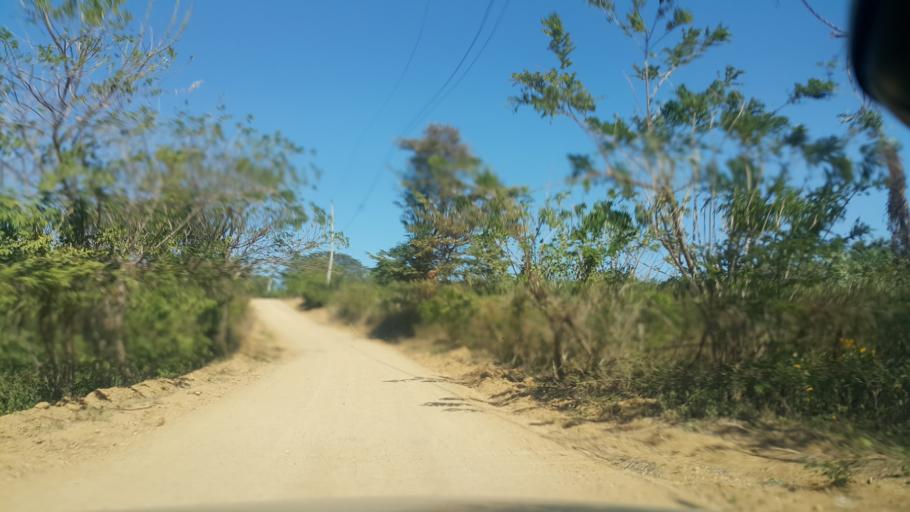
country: NI
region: Rivas
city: San Juan del Sur
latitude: 11.2818
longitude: -85.8832
